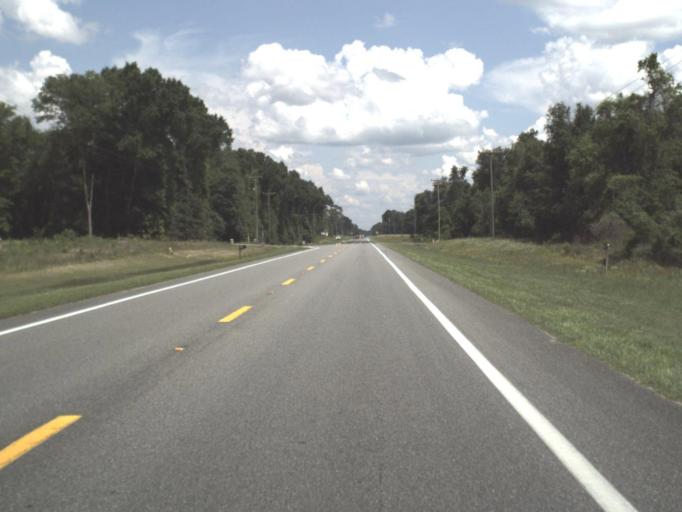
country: US
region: Florida
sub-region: Alachua County
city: High Springs
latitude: 29.9142
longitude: -82.7048
